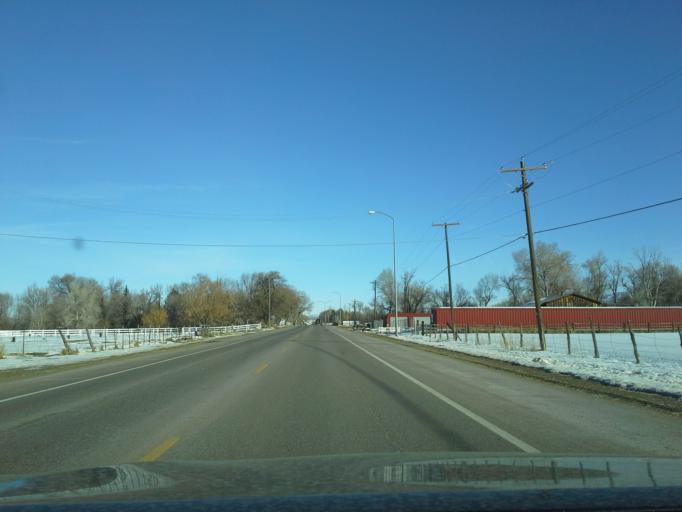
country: US
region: Utah
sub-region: Beaver County
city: Beaver
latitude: 38.2629
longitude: -112.6446
